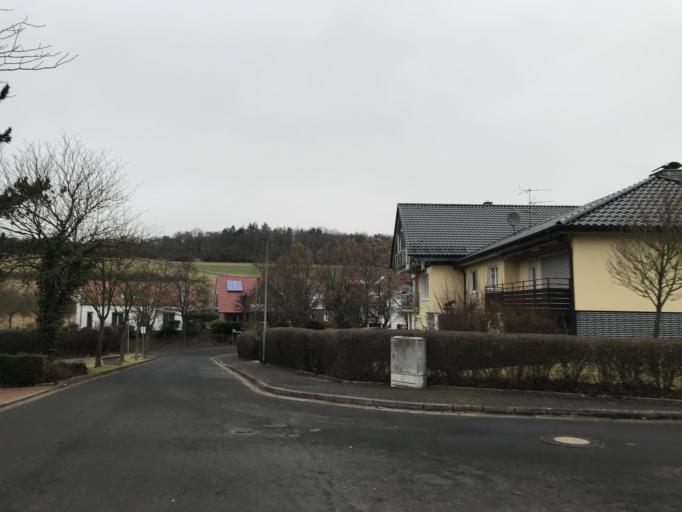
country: DE
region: Hesse
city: Fritzlar
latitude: 51.1307
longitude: 9.2629
